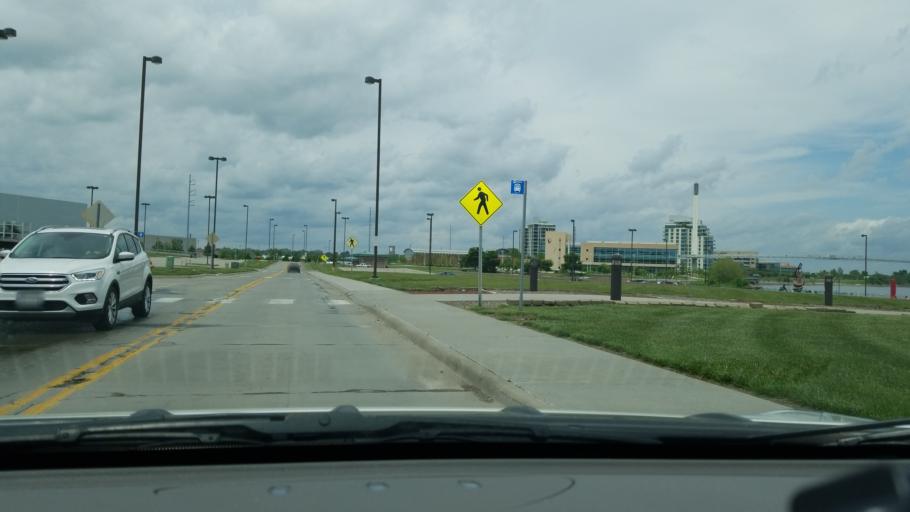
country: US
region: Nebraska
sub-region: Douglas County
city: Omaha
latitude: 41.2614
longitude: -95.9242
